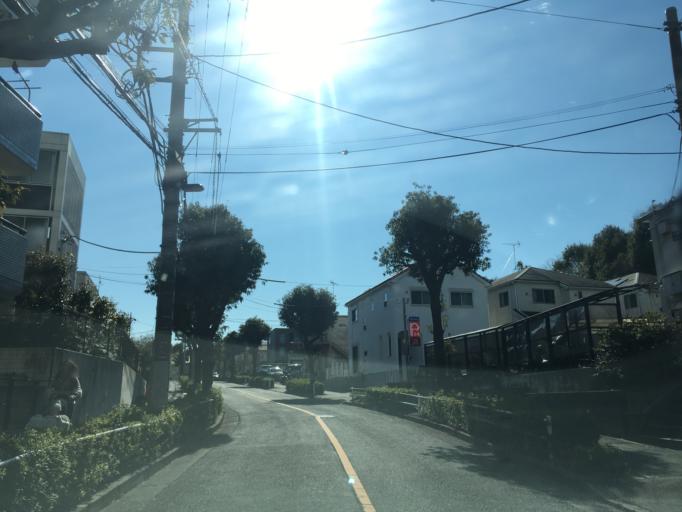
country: JP
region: Tokyo
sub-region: Machida-shi
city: Machida
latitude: 35.6089
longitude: 139.4332
